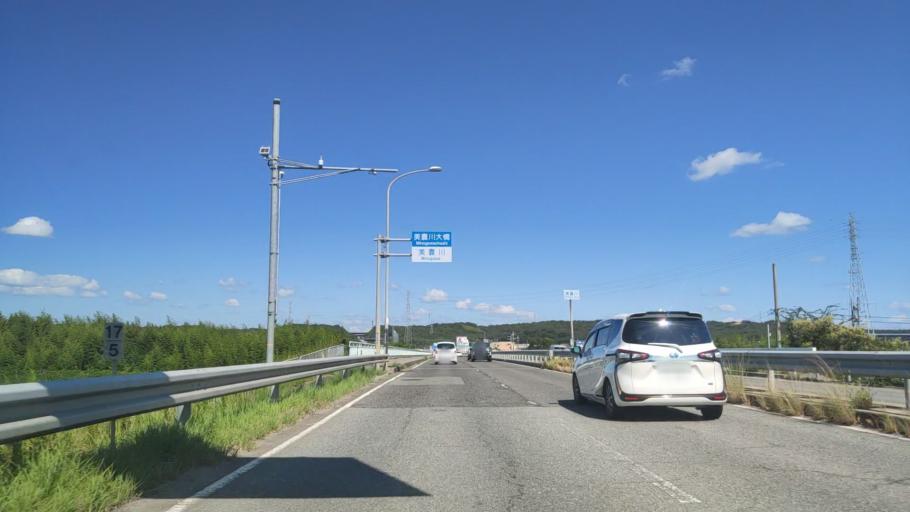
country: JP
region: Hyogo
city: Miki
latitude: 34.7994
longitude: 134.9665
